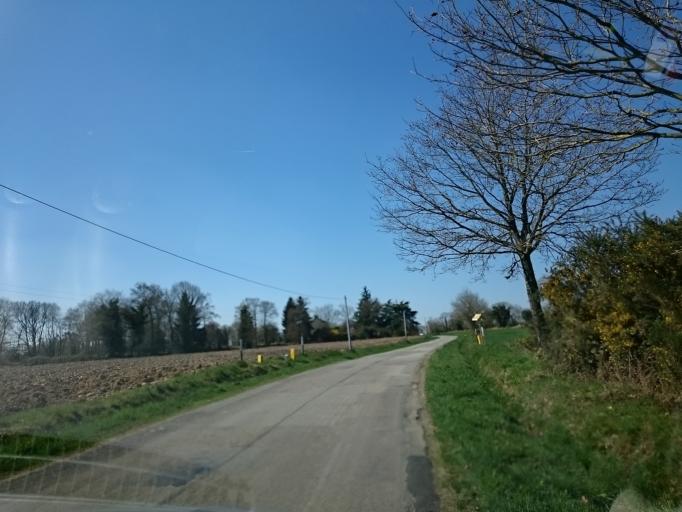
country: FR
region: Brittany
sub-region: Departement d'Ille-et-Vilaine
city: Crevin
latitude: 47.9624
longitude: -1.6746
